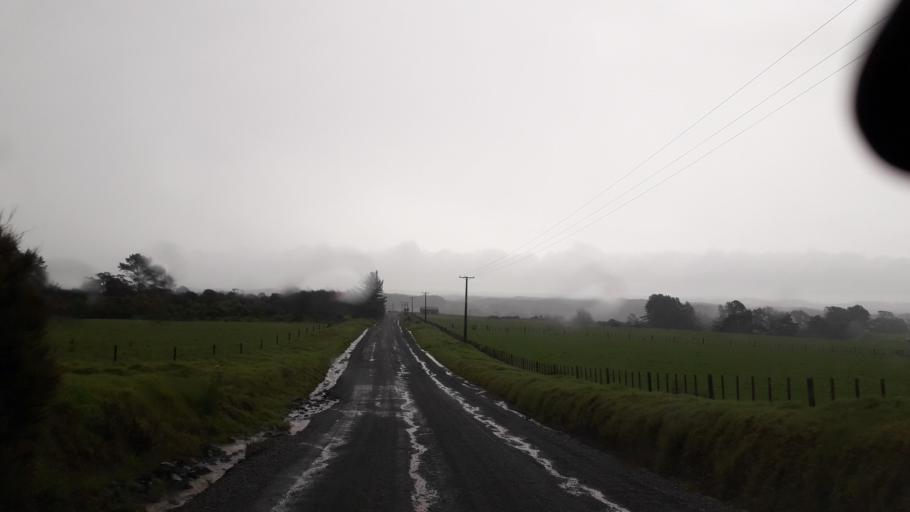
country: NZ
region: Northland
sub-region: Far North District
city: Kerikeri
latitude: -35.1305
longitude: 174.0043
